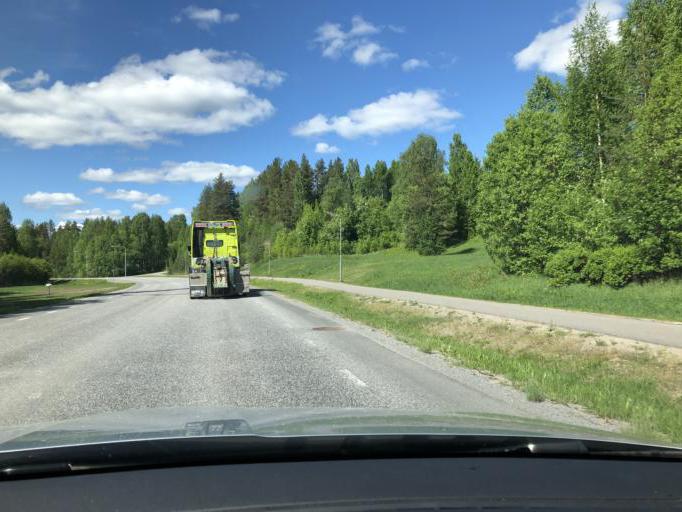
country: SE
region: Norrbotten
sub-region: Alvsbyns Kommun
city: AElvsbyn
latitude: 65.6669
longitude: 21.0266
